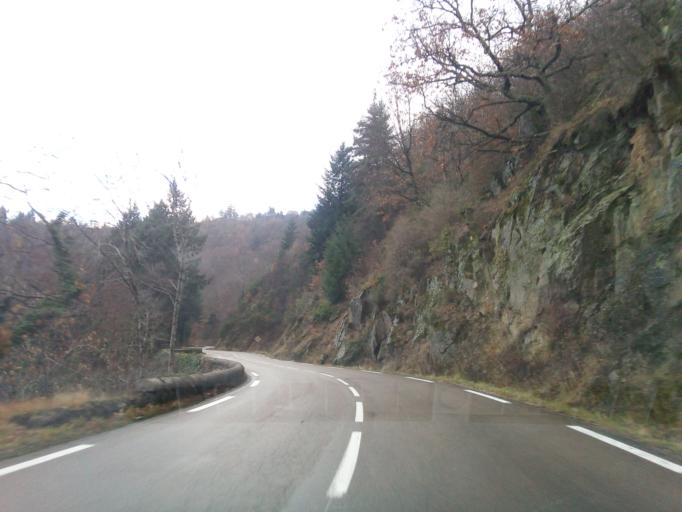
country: FR
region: Rhone-Alpes
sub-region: Departement de l'Ardeche
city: Le Cheylard
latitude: 44.8816
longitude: 4.5097
